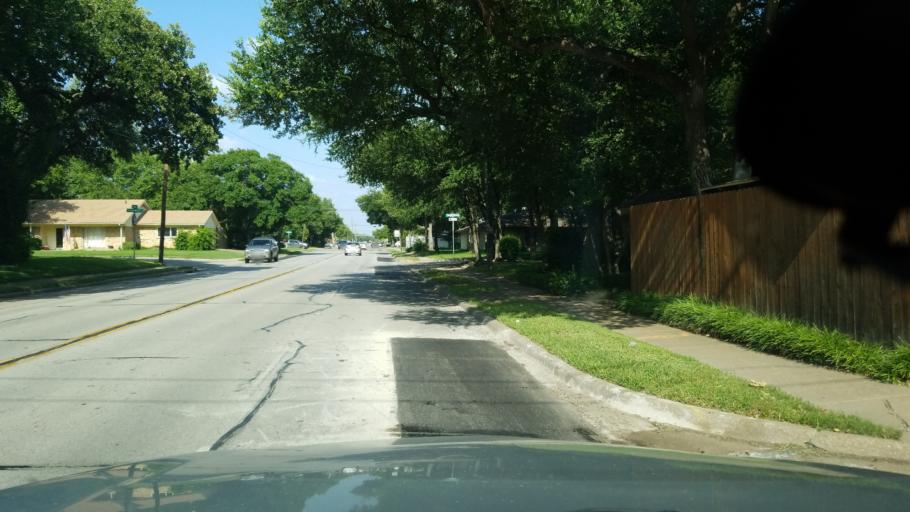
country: US
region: Texas
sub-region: Dallas County
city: Irving
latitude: 32.8224
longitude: -96.9721
